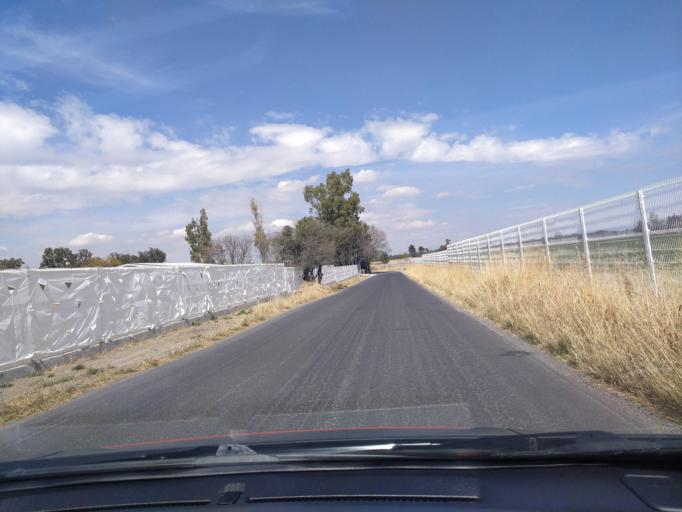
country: MX
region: Guanajuato
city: San Roque
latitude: 20.9654
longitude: -101.8294
